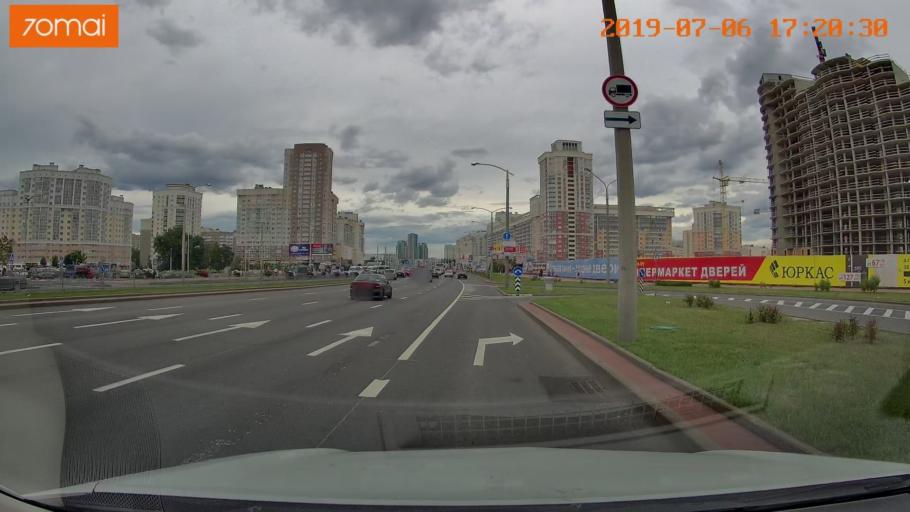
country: BY
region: Minsk
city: Shchomyslitsa
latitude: 53.8444
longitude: 27.4758
